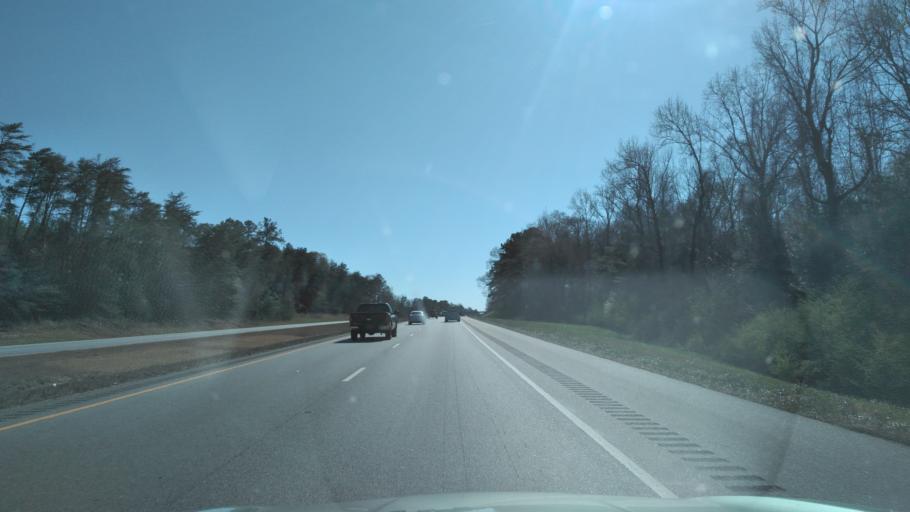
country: US
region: Alabama
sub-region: Lowndes County
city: Fort Deposit
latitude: 31.9162
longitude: -86.5821
